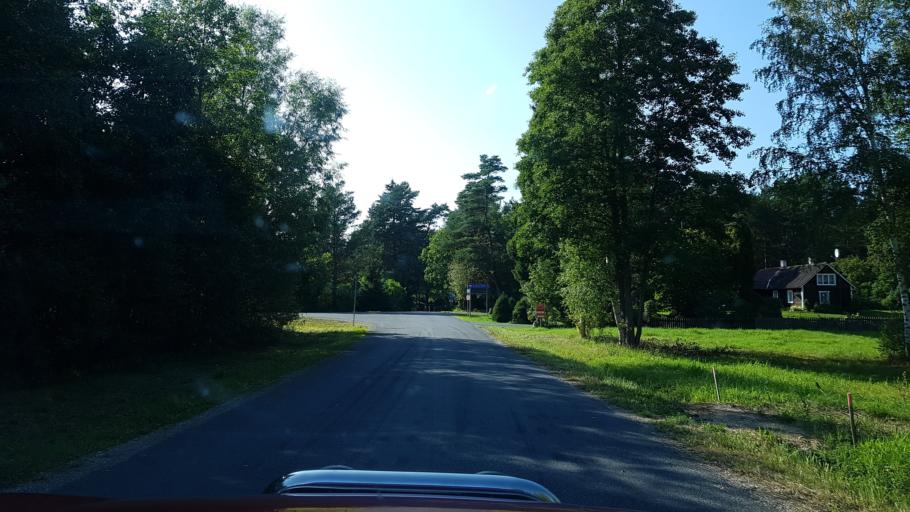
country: EE
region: Harju
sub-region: Paldiski linn
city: Paldiski
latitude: 59.2764
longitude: 24.0305
